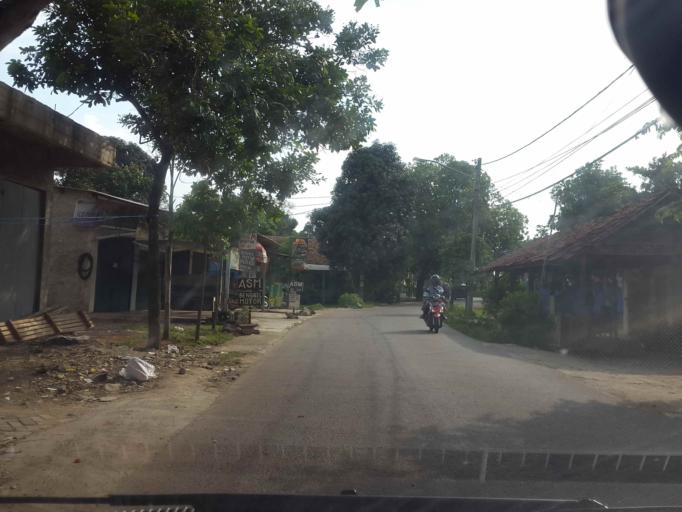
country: ID
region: West Java
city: Ciputat
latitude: -6.2635
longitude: 106.6736
